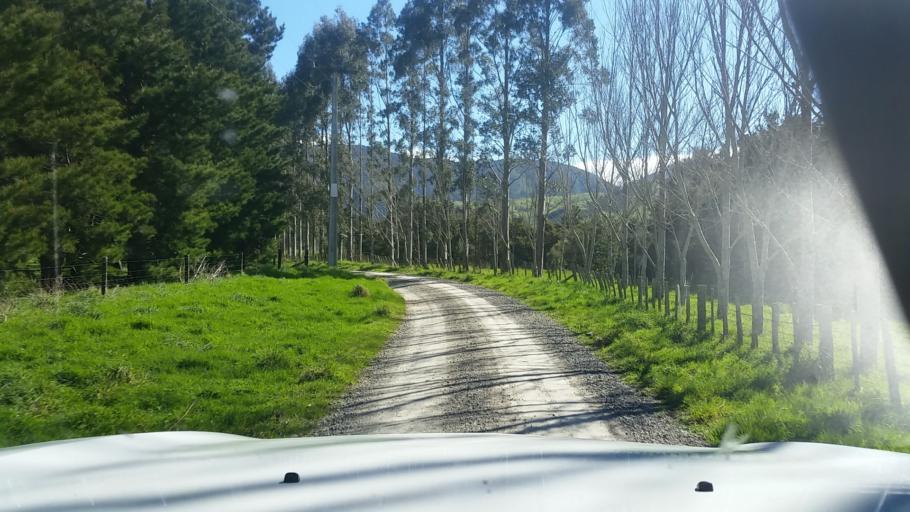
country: NZ
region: Wellington
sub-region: Masterton District
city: Masterton
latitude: -40.8873
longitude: 175.5192
